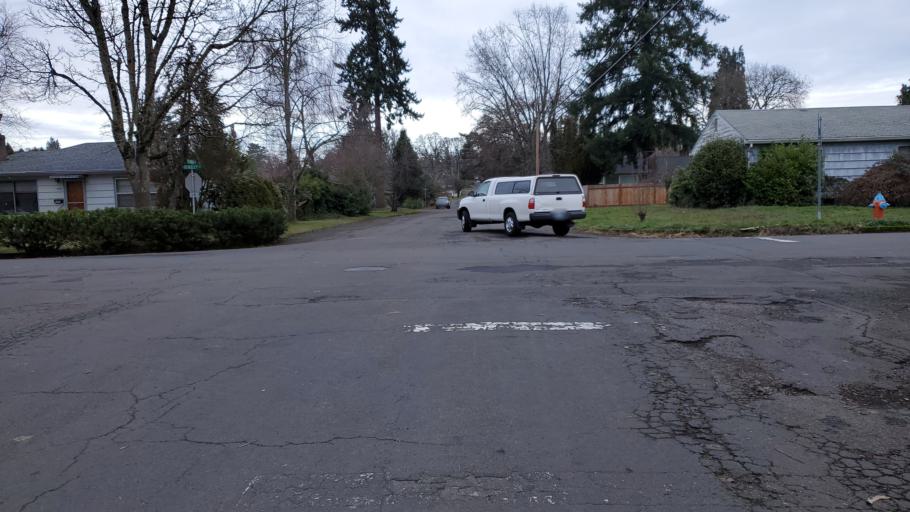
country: US
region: Oregon
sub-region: Clackamas County
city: Gladstone
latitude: 45.3815
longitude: -122.5855
